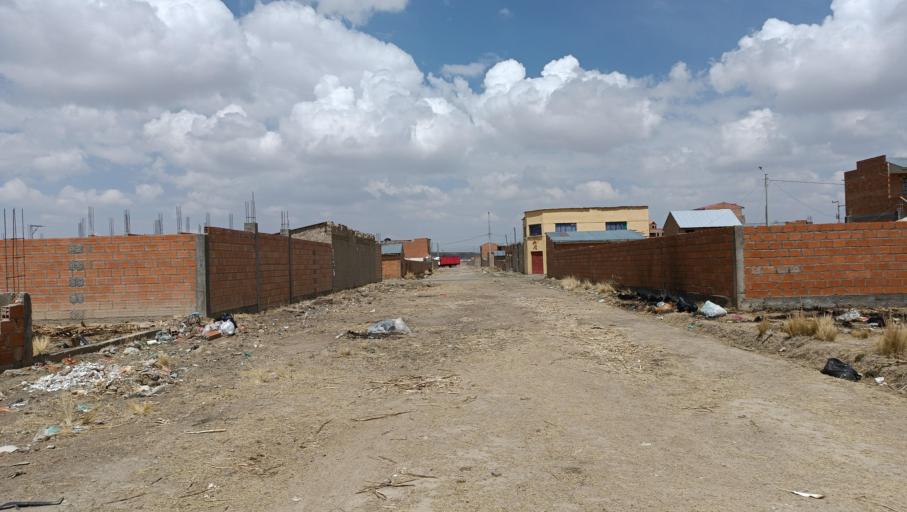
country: BO
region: La Paz
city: Batallas
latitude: -16.4068
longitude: -68.5401
